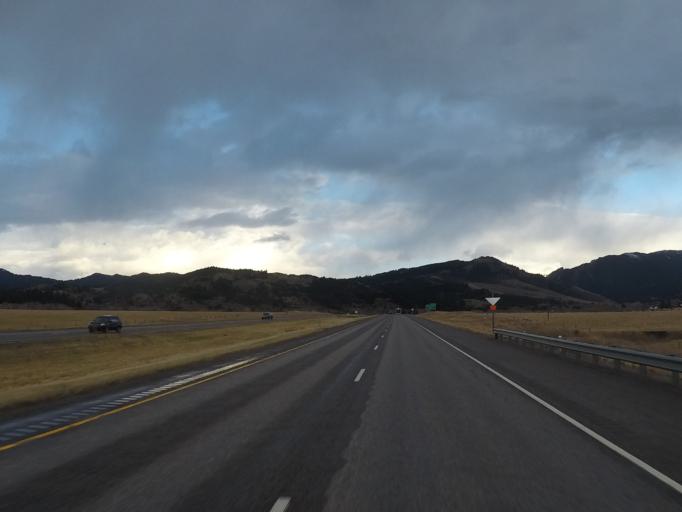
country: US
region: Montana
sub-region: Gallatin County
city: Bozeman
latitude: 45.6634
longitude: -110.9679
